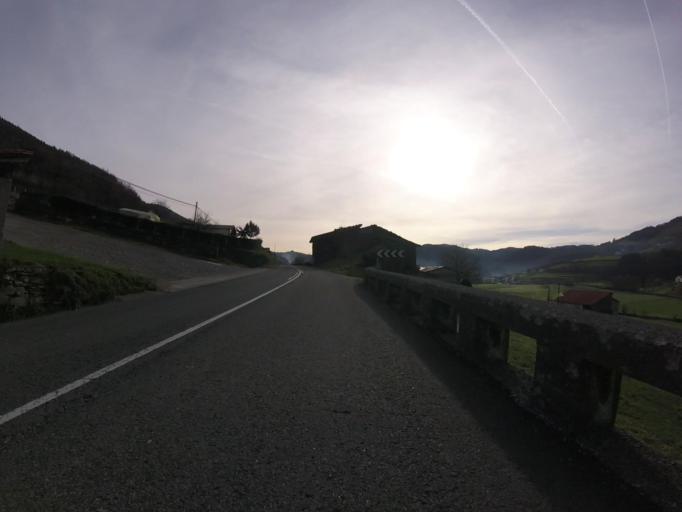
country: ES
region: Basque Country
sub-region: Provincia de Guipuzcoa
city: Berastegui
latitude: 43.1307
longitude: -1.9856
